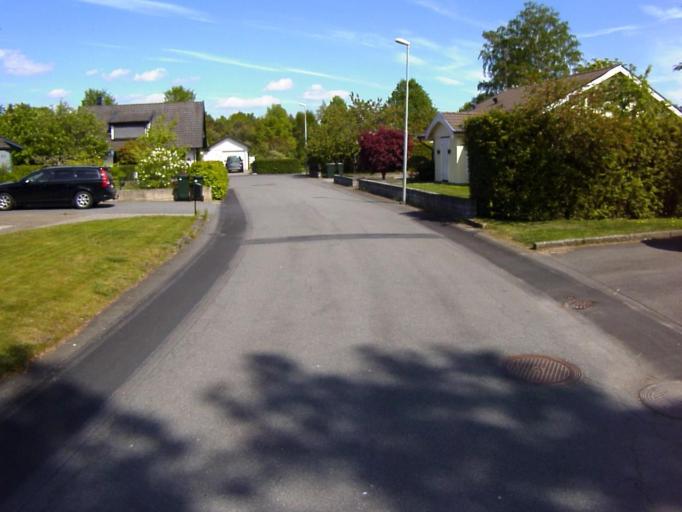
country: SE
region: Skane
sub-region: Kristianstads Kommun
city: Kristianstad
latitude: 56.0779
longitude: 14.0936
